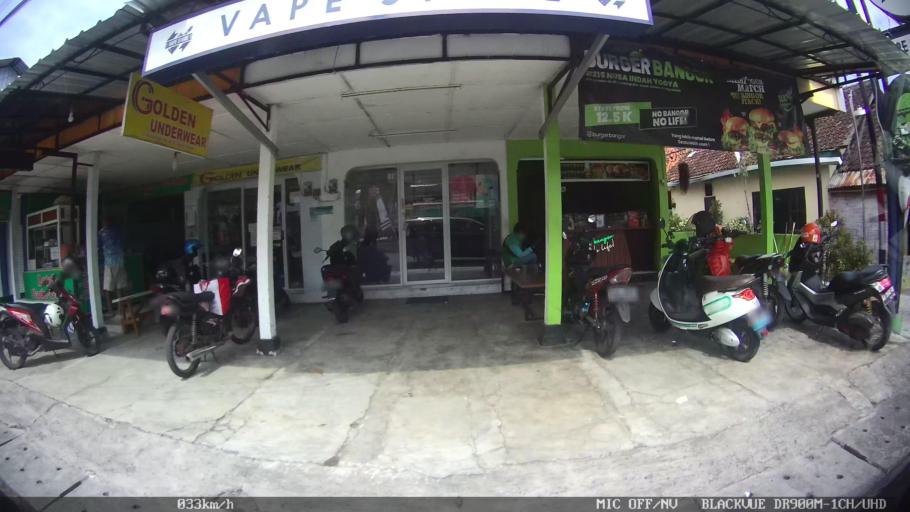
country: ID
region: Daerah Istimewa Yogyakarta
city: Depok
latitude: -7.7571
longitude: 110.4092
